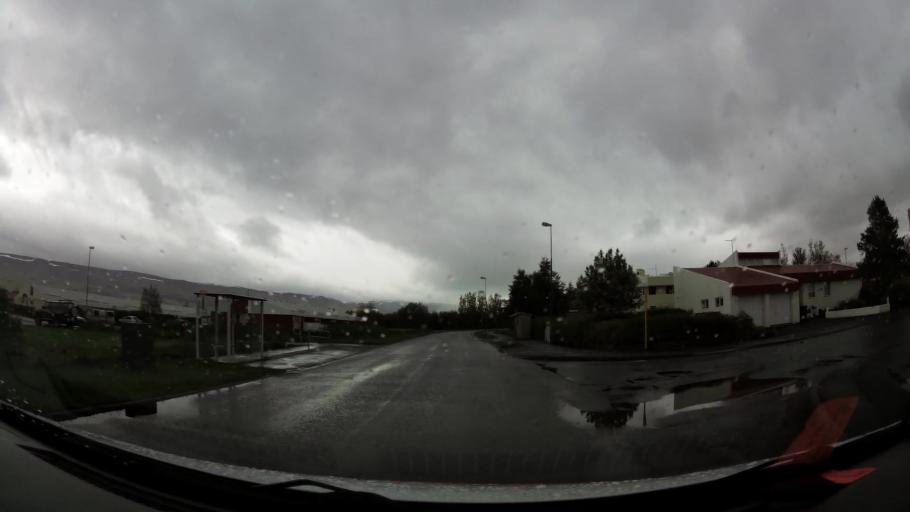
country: IS
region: Northeast
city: Akureyri
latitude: 65.6946
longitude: -18.1443
